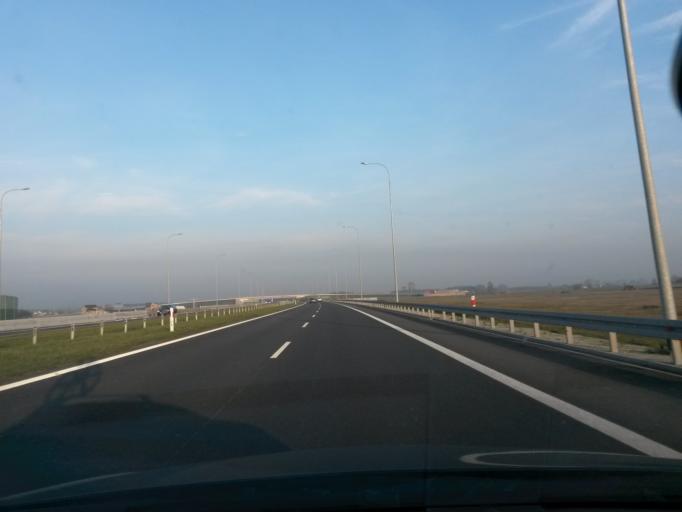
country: PL
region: Greater Poland Voivodeship
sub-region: Powiat kepinski
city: Baranow
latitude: 51.3212
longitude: 18.0651
